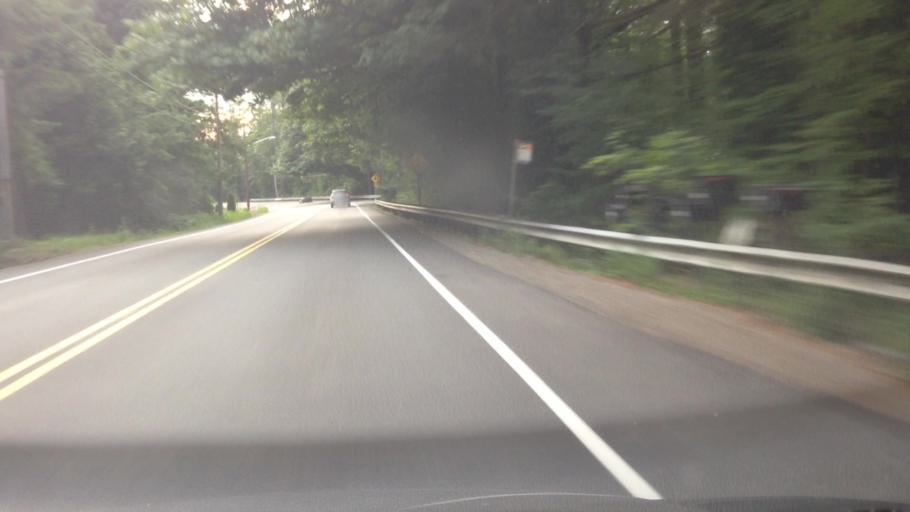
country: US
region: Washington
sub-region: King County
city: Cottage Lake
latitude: 47.7603
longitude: -122.0346
